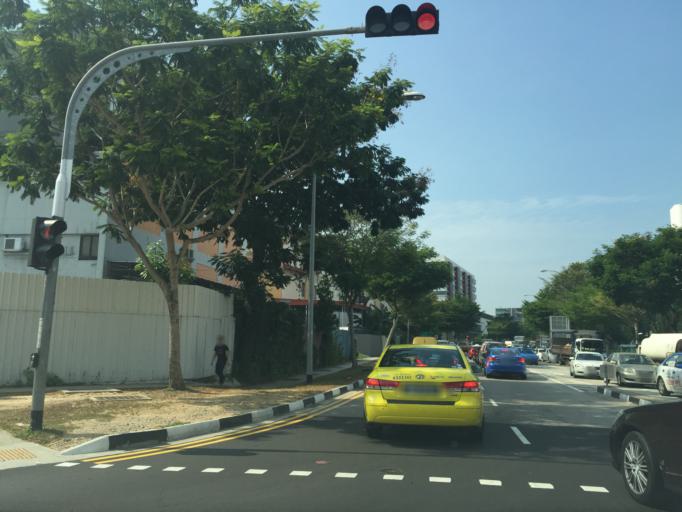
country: SG
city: Singapore
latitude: 1.3356
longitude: 103.8940
